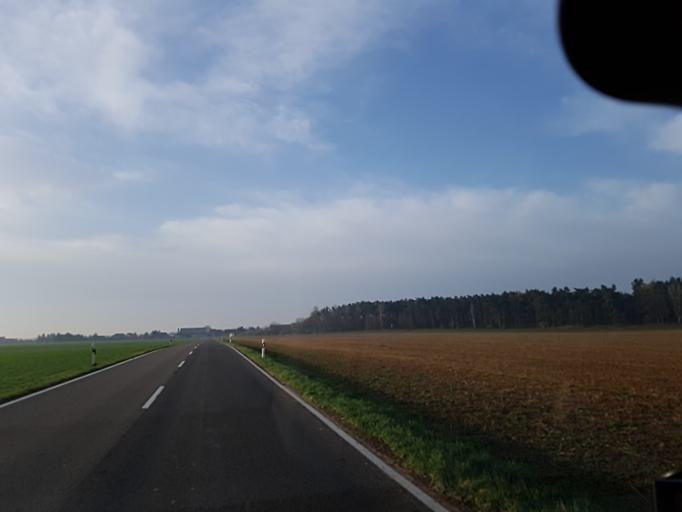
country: DE
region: Saxony
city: Strehla
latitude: 51.3864
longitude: 13.2786
